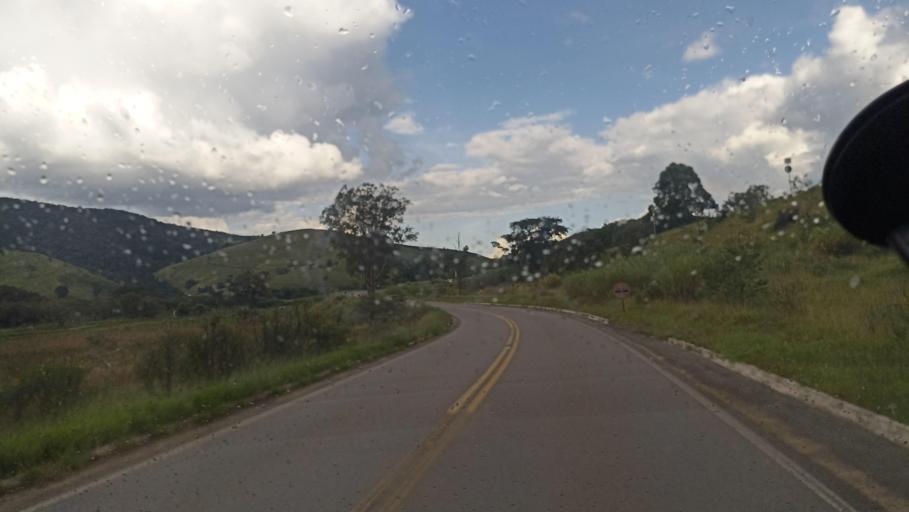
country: BR
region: Minas Gerais
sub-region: Baependi
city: Baependi
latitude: -21.9225
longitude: -44.8216
